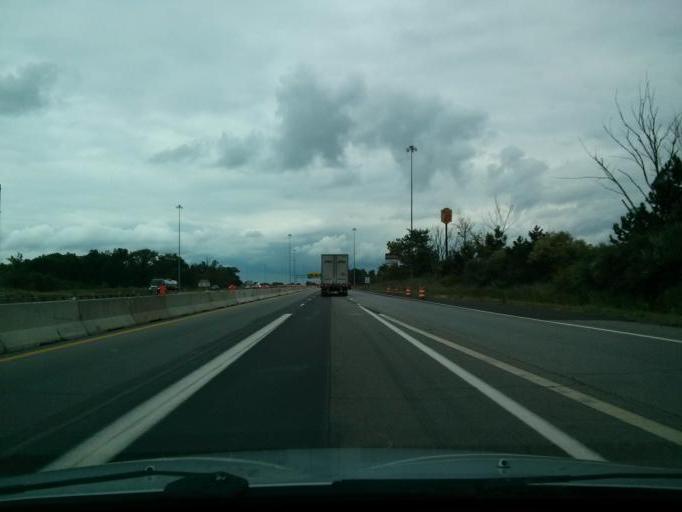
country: US
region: Ohio
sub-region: Trumbull County
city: Mineral Ridge
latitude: 41.1235
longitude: -80.7645
